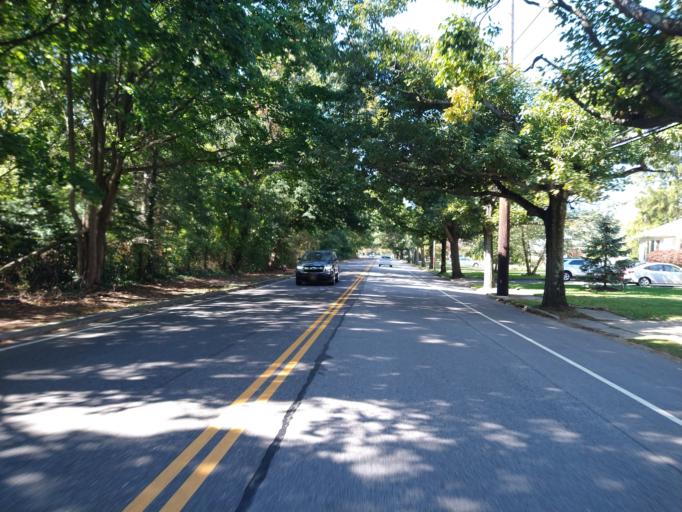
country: US
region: New York
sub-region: Nassau County
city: Woodbury
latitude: 40.8252
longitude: -73.4837
